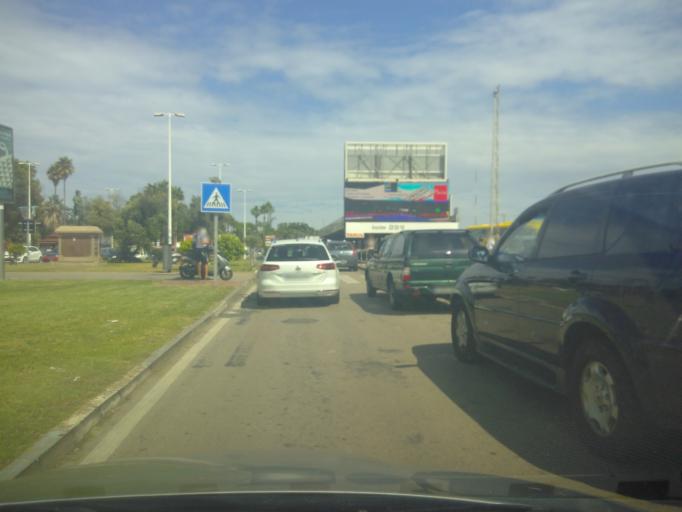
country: ES
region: Andalusia
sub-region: Provincia de Cadiz
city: La Linea de la Concepcion
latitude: 36.1561
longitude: -5.3486
